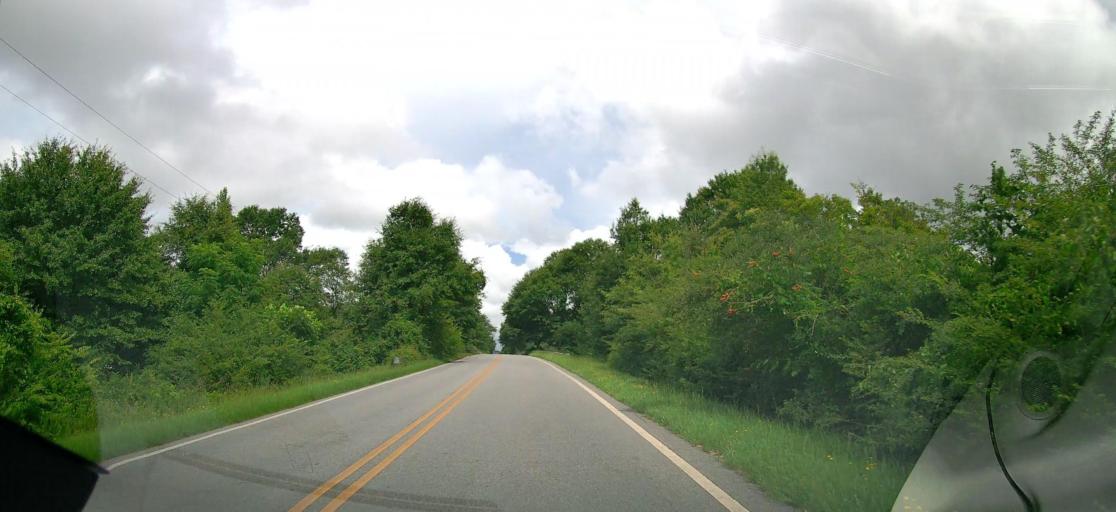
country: US
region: Georgia
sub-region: Peach County
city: Byron
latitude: 32.6422
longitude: -83.7424
